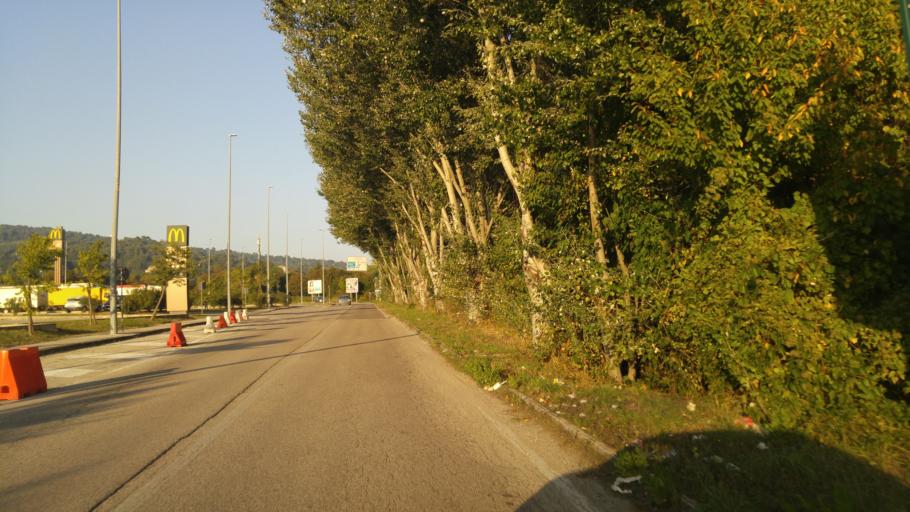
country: IT
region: The Marches
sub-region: Provincia di Pesaro e Urbino
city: Pesaro
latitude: 43.9061
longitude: 12.8722
